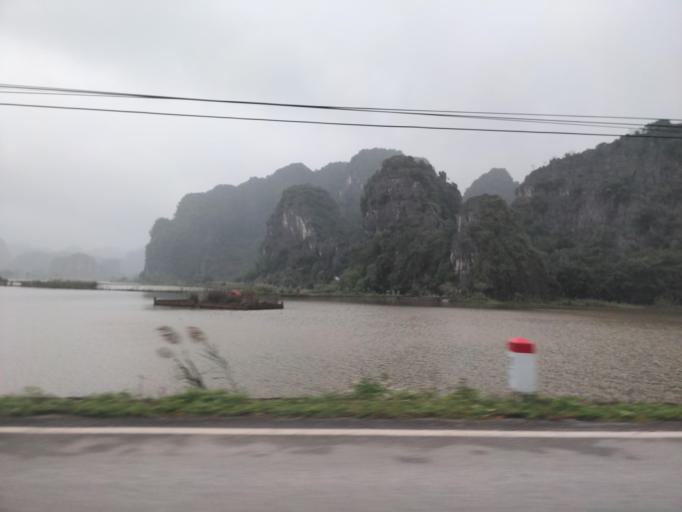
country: VN
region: Ninh Binh
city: Thi Tran Tam Diep
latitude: 20.2205
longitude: 105.9239
